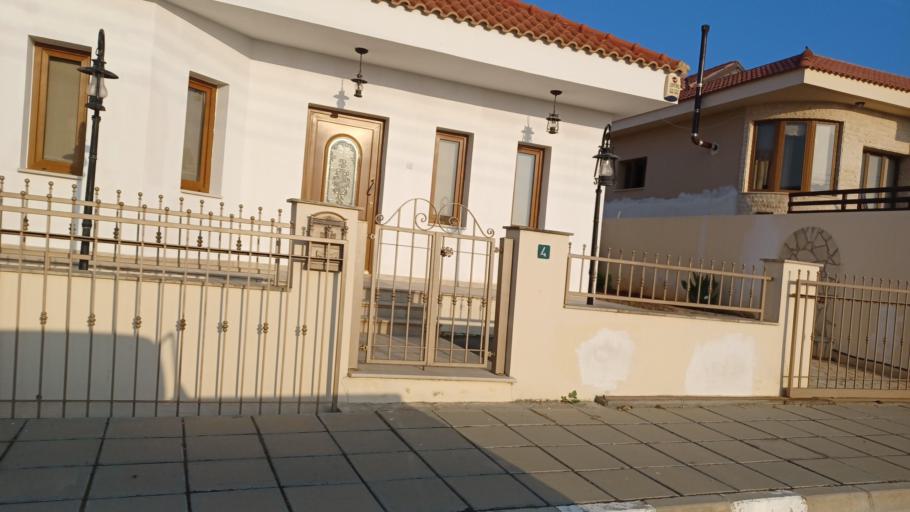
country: CY
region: Larnaka
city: Pyla
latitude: 35.0054
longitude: 33.6844
